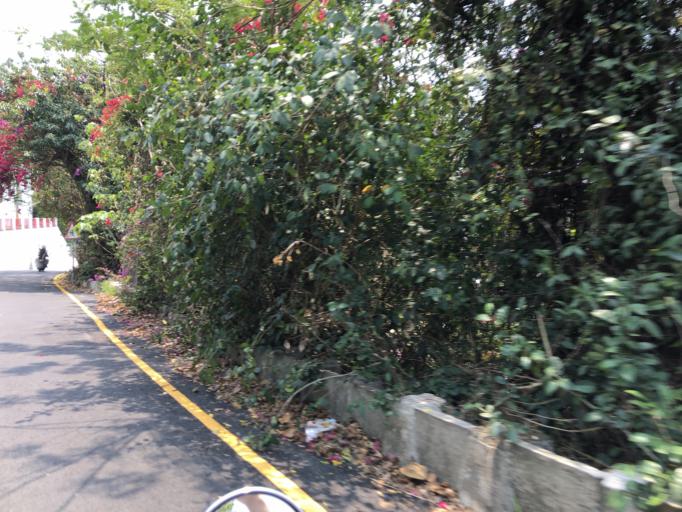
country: TW
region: Kaohsiung
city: Kaohsiung
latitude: 22.6254
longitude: 120.2725
